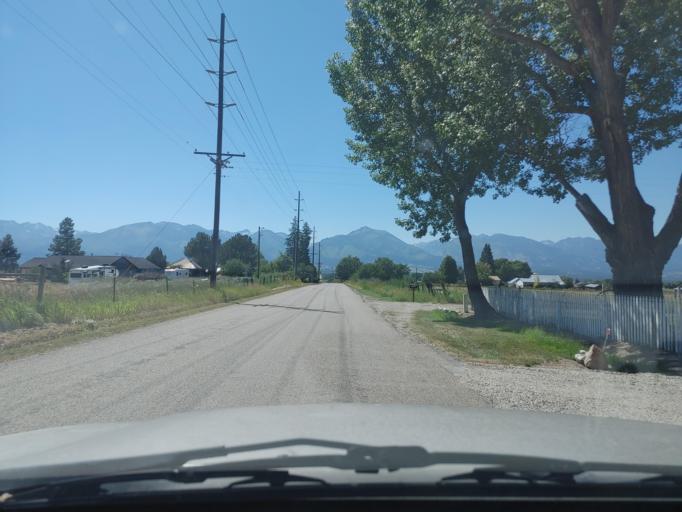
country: US
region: Montana
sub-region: Ravalli County
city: Hamilton
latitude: 46.2768
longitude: -114.0477
